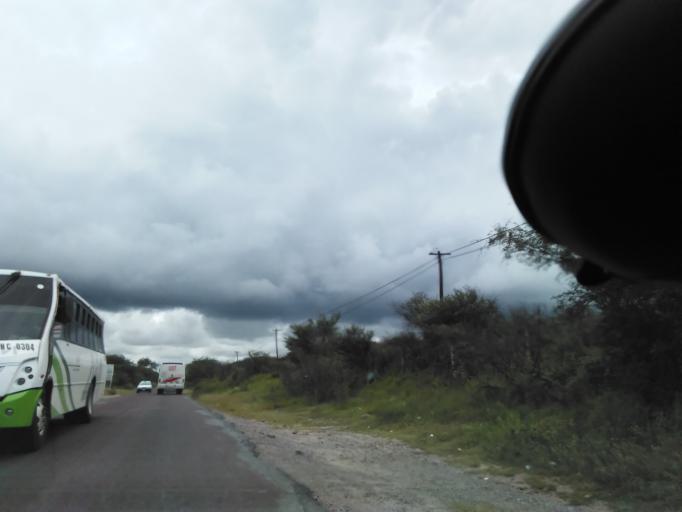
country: MX
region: Hidalgo
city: Tula de Allende
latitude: 20.0596
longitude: -99.3568
